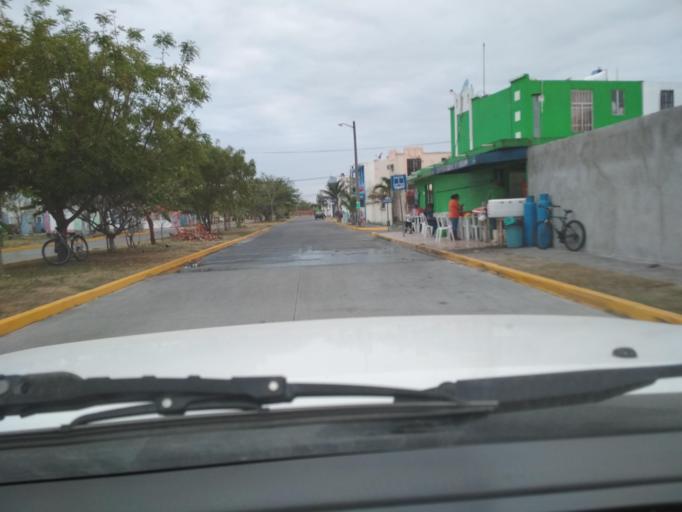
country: MX
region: Veracruz
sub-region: Medellin
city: Fraccionamiento Arboledas San Ramon
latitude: 19.0928
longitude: -96.1555
